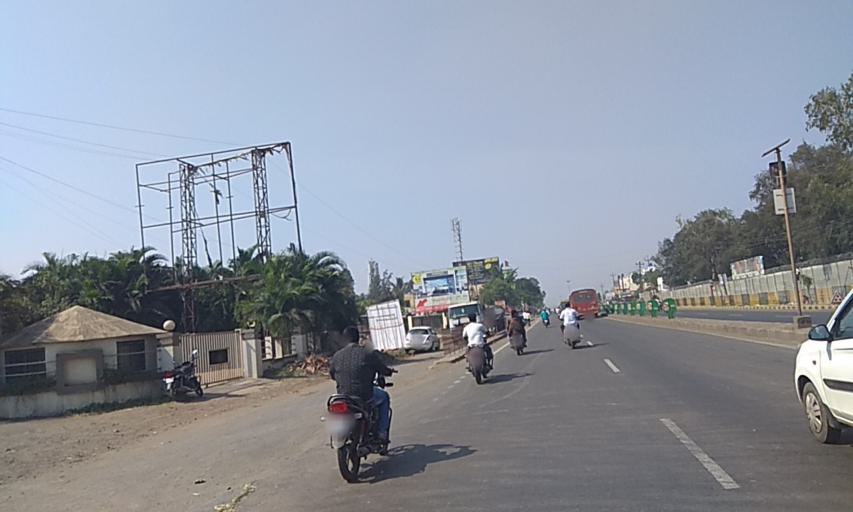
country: IN
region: Maharashtra
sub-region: Pune Division
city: Lohogaon
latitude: 18.4907
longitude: 74.0102
